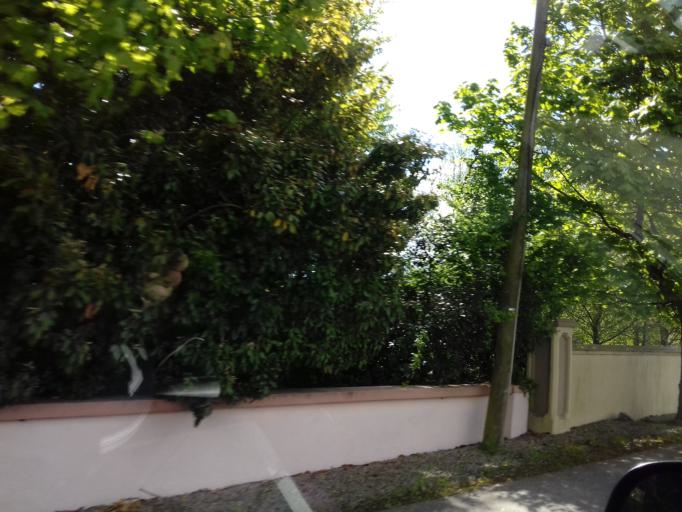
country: IE
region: Leinster
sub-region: Loch Garman
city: Castlebridge
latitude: 52.3782
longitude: -6.4507
